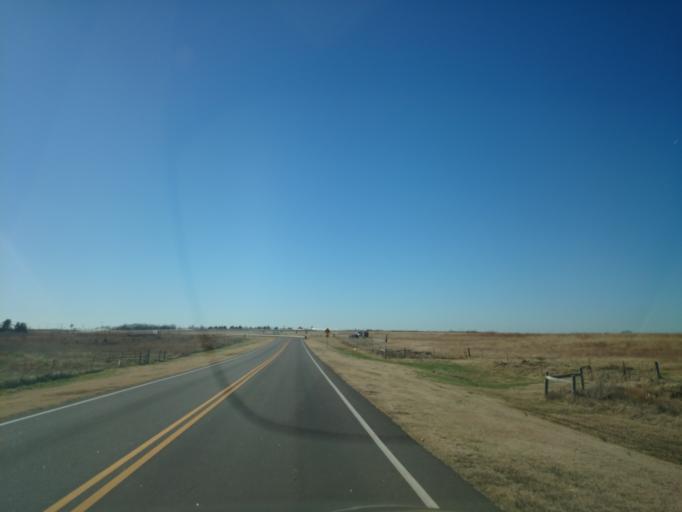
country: US
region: Oklahoma
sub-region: Payne County
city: Stillwater
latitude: 36.1520
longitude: -97.0837
